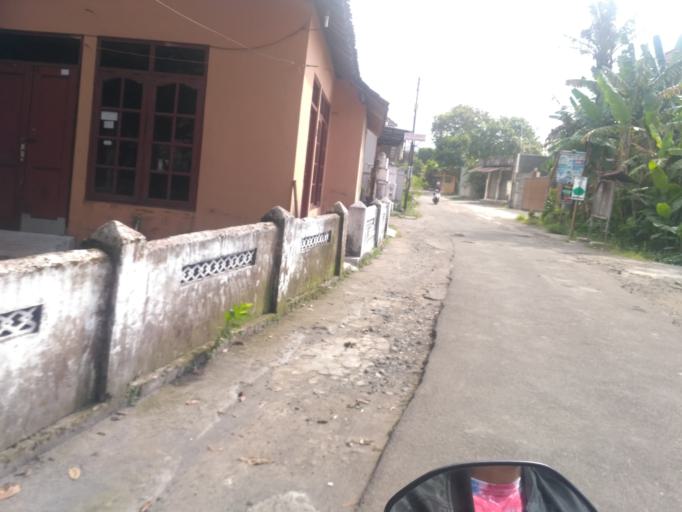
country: ID
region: Daerah Istimewa Yogyakarta
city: Yogyakarta
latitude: -7.7601
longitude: 110.3585
